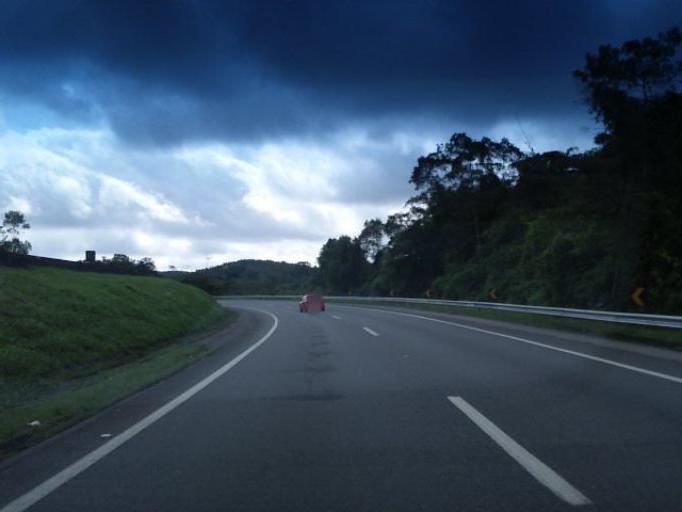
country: BR
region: Parana
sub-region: Antonina
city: Antonina
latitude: -25.0985
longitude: -48.6867
